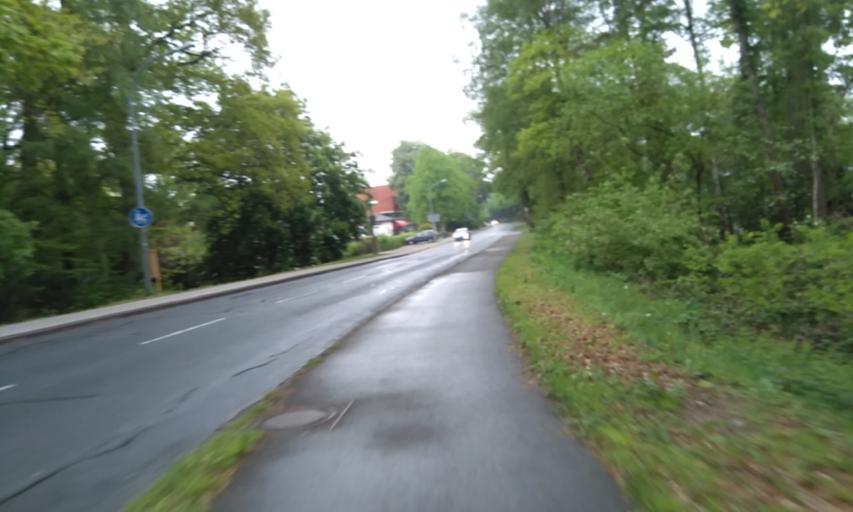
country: DE
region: Lower Saxony
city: Buxtehude
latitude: 53.4700
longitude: 9.6726
